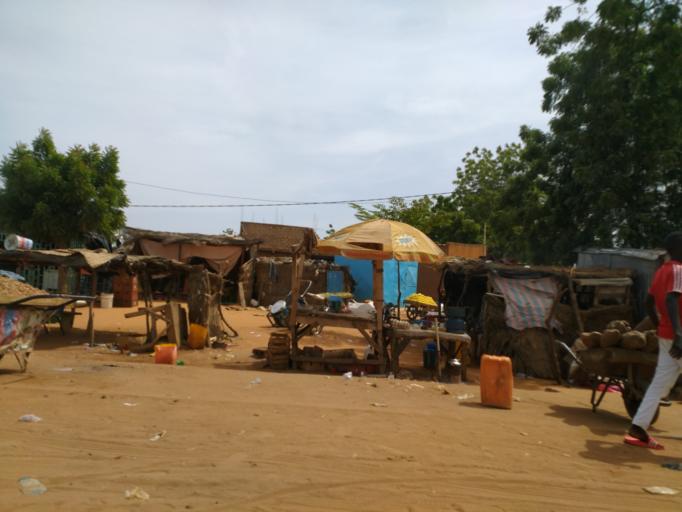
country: NE
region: Niamey
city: Niamey
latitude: 13.5329
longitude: 2.0803
